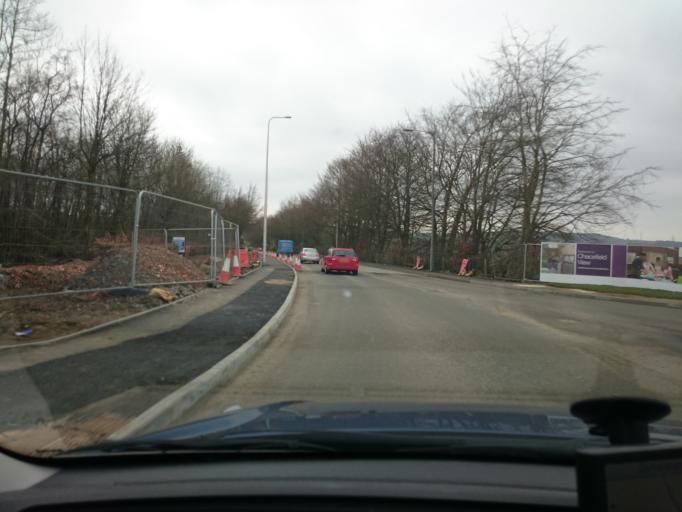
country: GB
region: Scotland
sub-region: Falkirk
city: Denny
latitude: 56.0127
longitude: -3.9063
